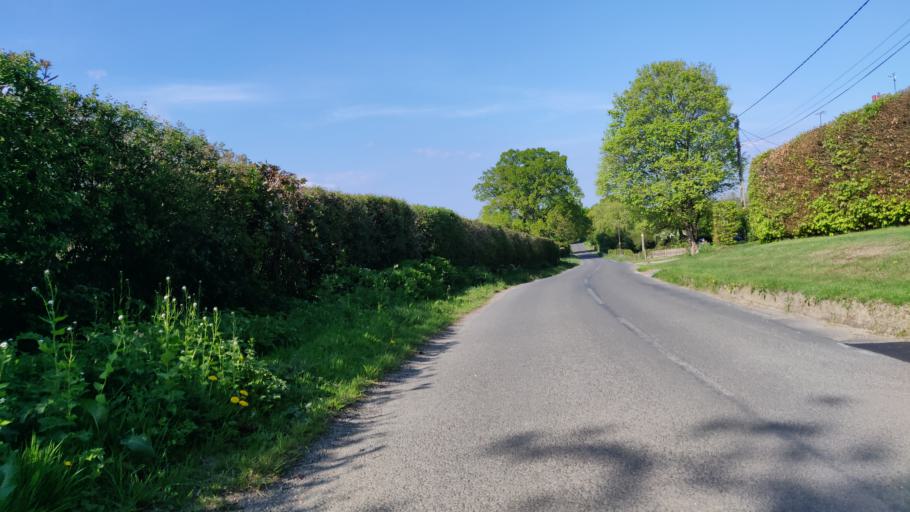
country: GB
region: England
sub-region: West Sussex
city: Southwater
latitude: 51.0424
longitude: -0.3567
